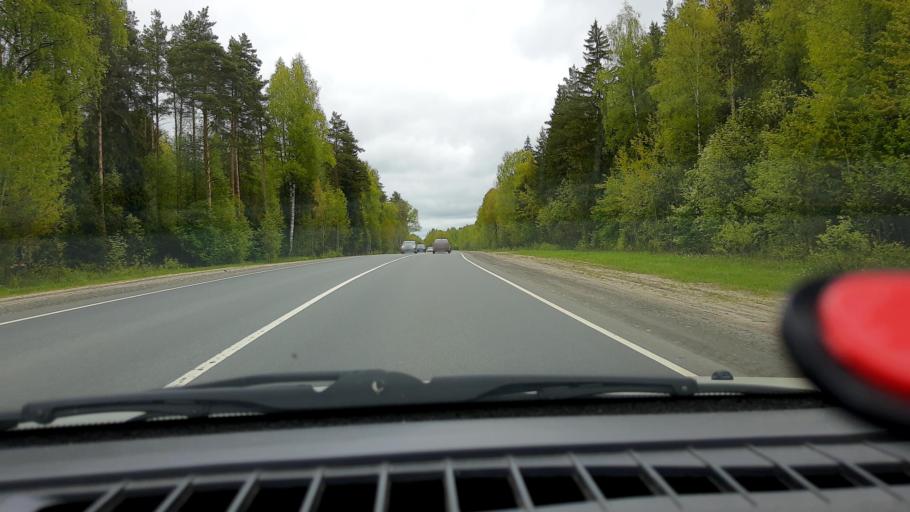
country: RU
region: Nizjnij Novgorod
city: Linda
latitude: 56.6402
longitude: 44.1074
